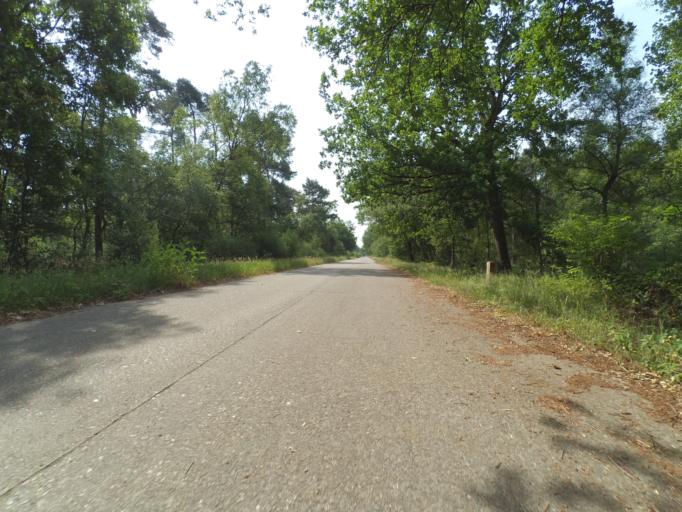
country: BE
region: Flanders
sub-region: Provincie Antwerpen
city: Kalmthout
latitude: 51.3514
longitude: 4.4934
